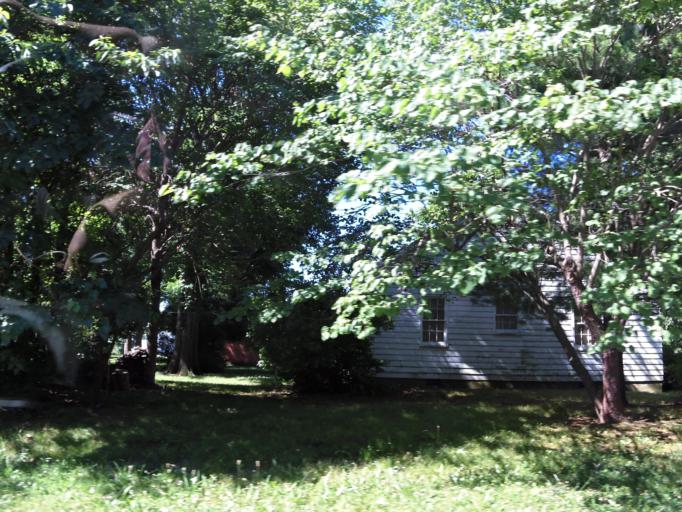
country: US
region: Arkansas
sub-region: Clay County
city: Piggott
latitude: 36.3844
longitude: -90.1904
